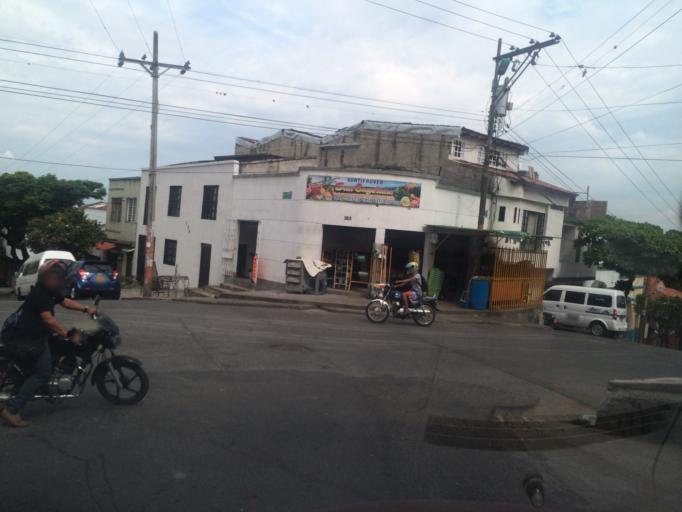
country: CO
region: Valle del Cauca
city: Cali
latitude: 3.4437
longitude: -76.5415
